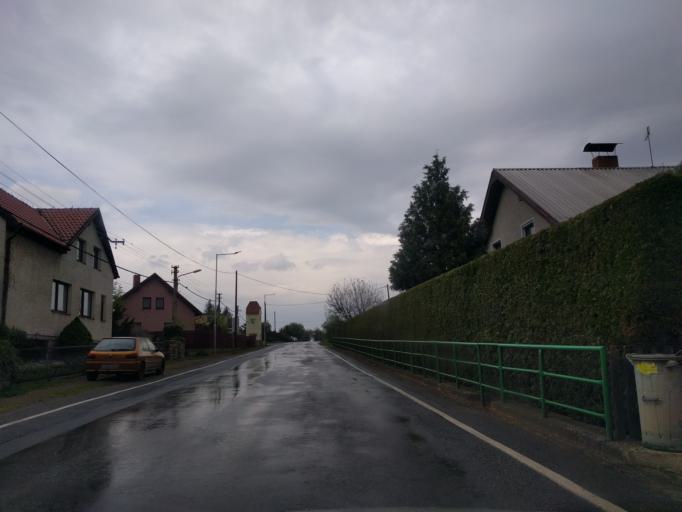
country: CZ
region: Central Bohemia
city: Dobris
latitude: 49.7444
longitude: 14.1519
